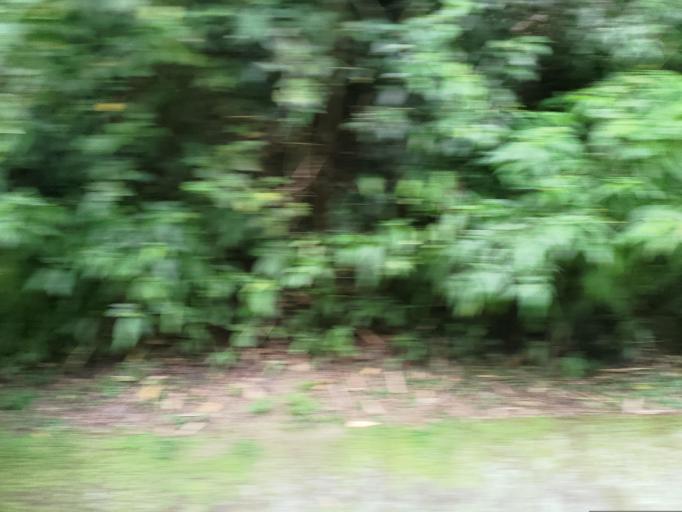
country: TW
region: Taiwan
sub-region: Hsinchu
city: Hsinchu
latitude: 24.6022
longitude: 121.0379
